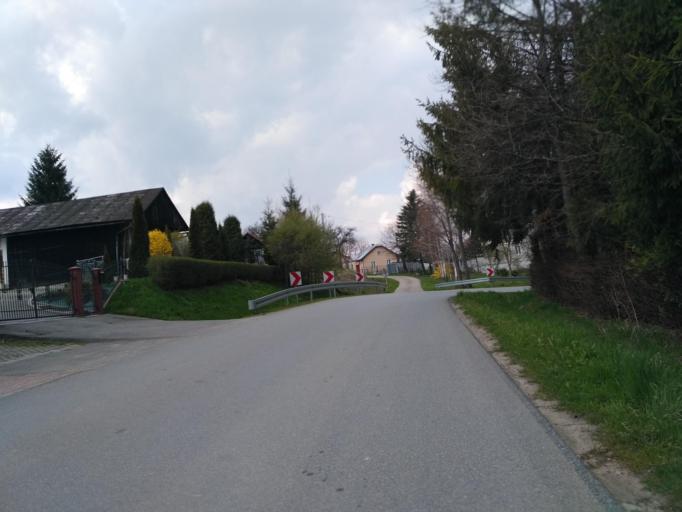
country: PL
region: Subcarpathian Voivodeship
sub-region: Powiat sanocki
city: Strachocina
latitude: 49.6061
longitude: 22.0890
